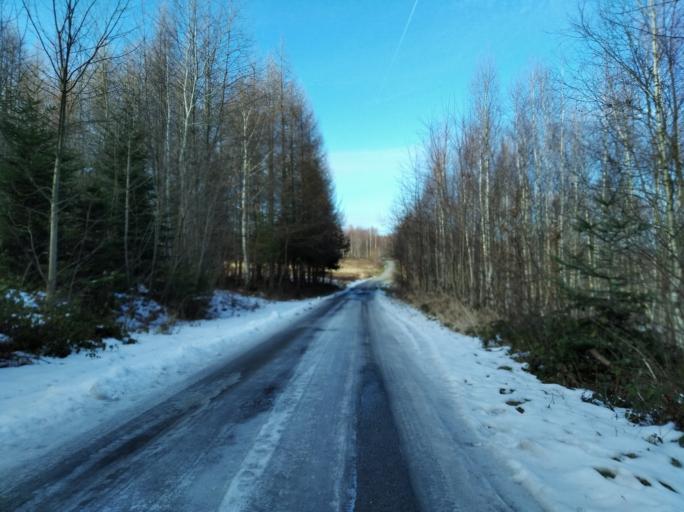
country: PL
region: Subcarpathian Voivodeship
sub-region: Powiat strzyzowski
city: Gwoznica Gorna
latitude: 49.8201
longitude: 21.9892
